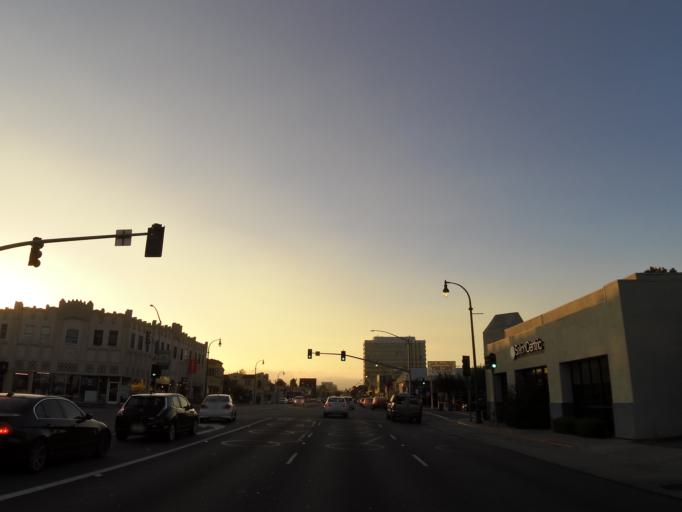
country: US
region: California
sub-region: San Mateo County
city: San Mateo
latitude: 37.5442
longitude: -122.3053
